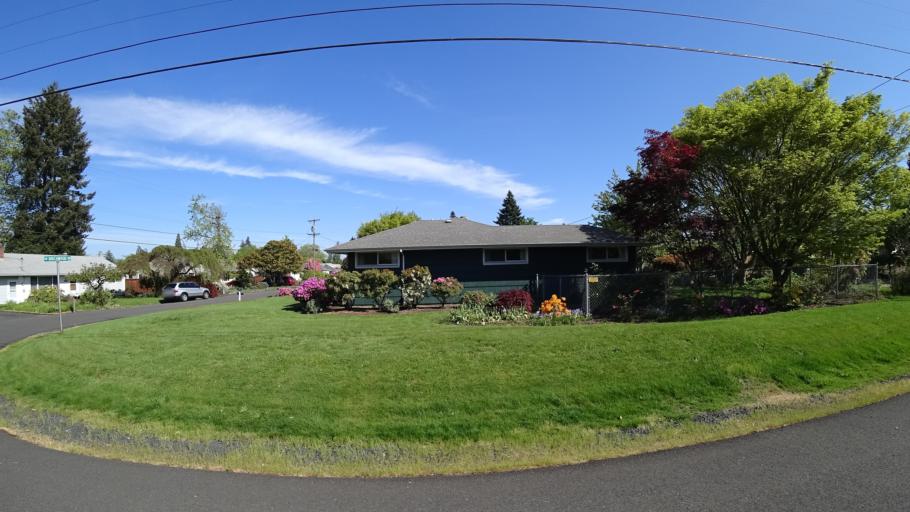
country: US
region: Oregon
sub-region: Washington County
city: Hillsboro
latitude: 45.5268
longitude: -122.9748
